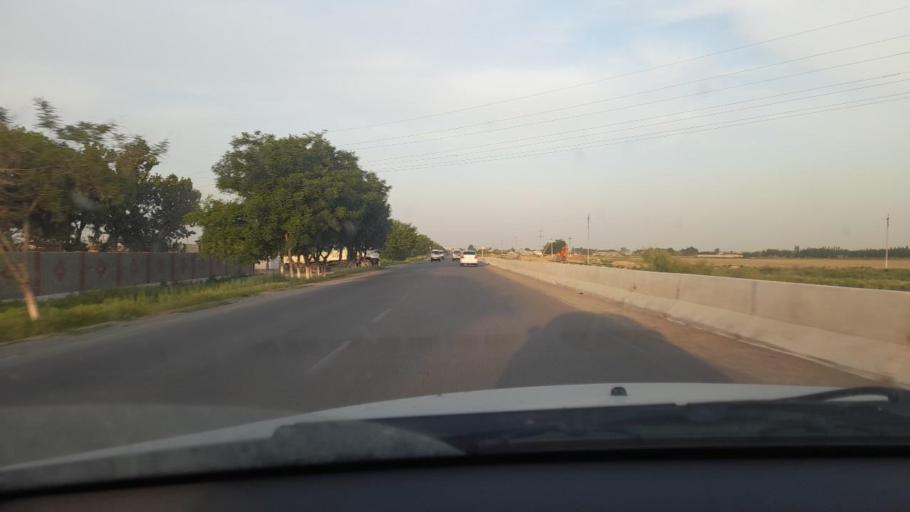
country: UZ
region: Sirdaryo
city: Guliston
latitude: 40.5080
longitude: 68.7345
